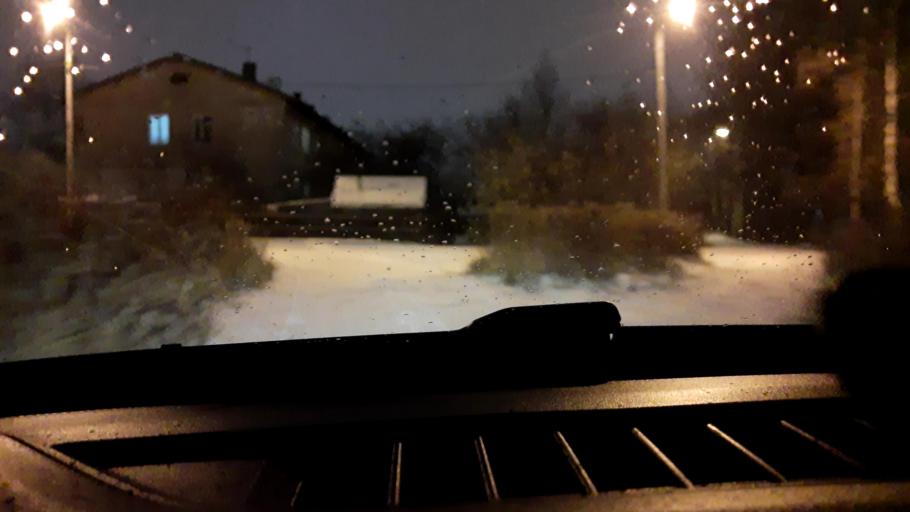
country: RU
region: Nizjnij Novgorod
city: Nizhniy Novgorod
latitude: 56.2949
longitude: 43.9212
